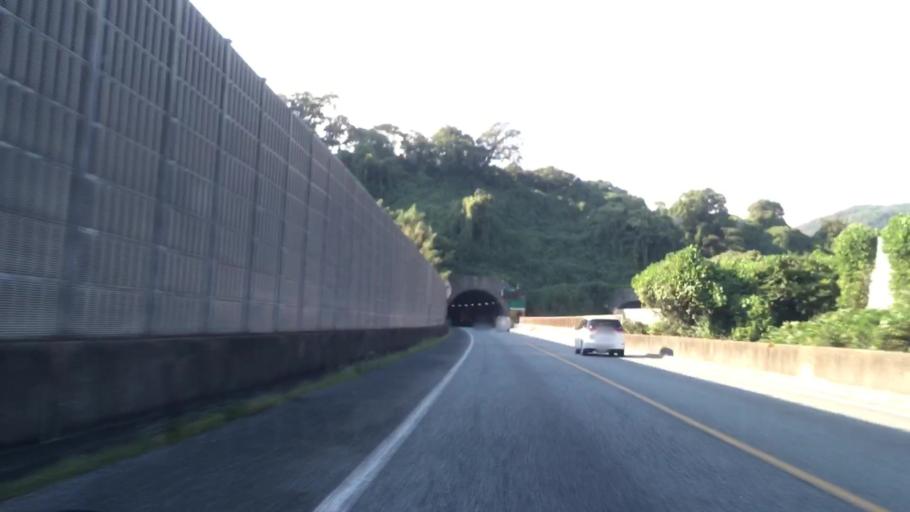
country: JP
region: Yamaguchi
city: Tokuyama
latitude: 34.0662
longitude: 131.8308
